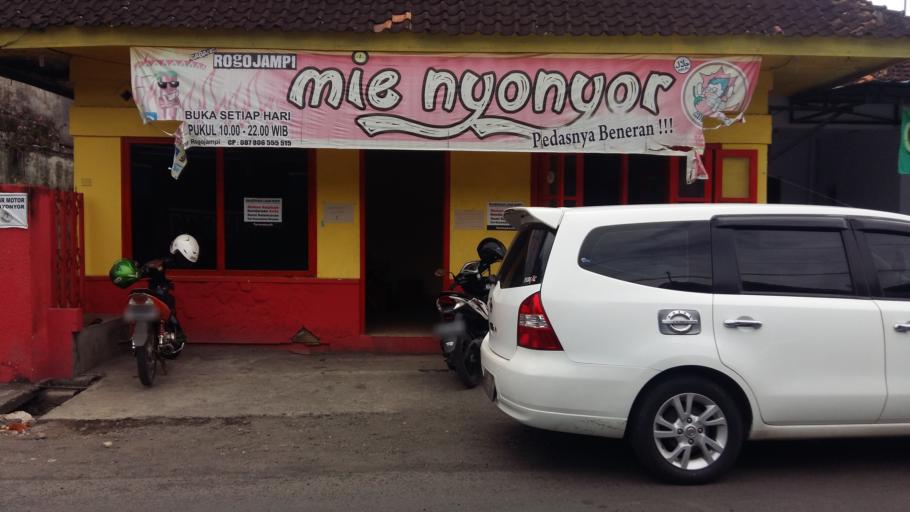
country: ID
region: East Java
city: Krajan
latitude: -8.3088
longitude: 114.2912
